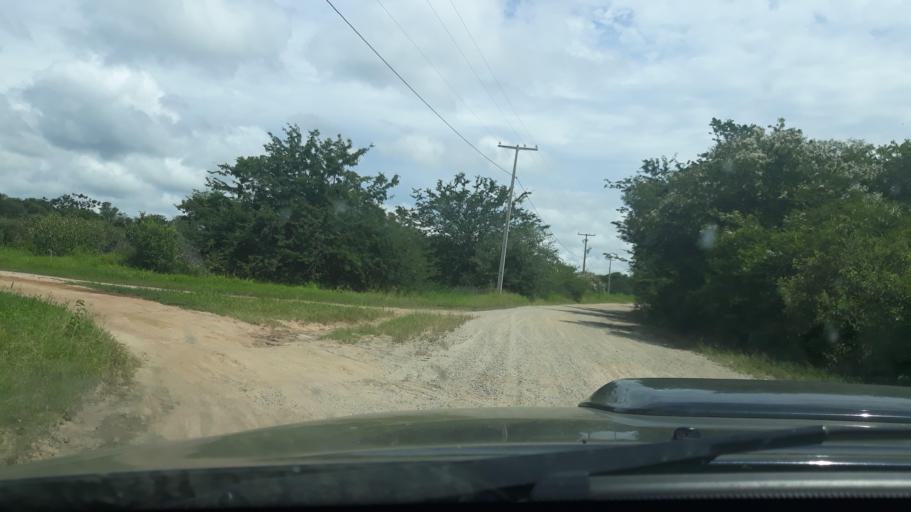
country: BR
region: Bahia
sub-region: Riacho De Santana
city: Riacho de Santana
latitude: -13.8760
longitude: -43.0206
